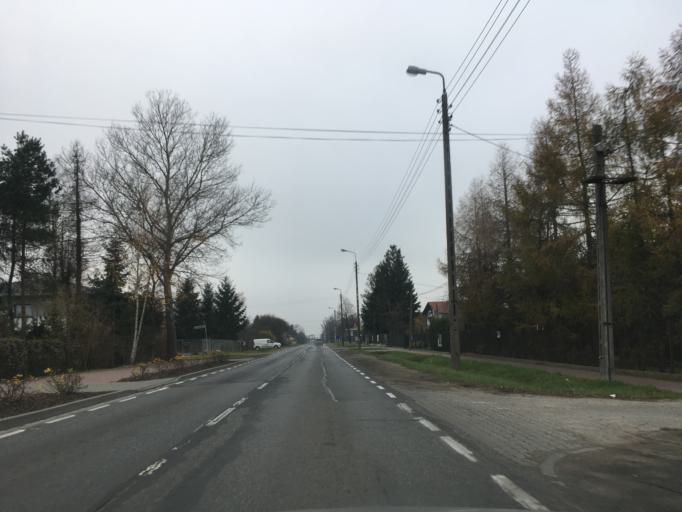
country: PL
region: Masovian Voivodeship
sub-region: Powiat piaseczynski
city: Piaseczno
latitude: 52.0821
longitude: 20.9920
